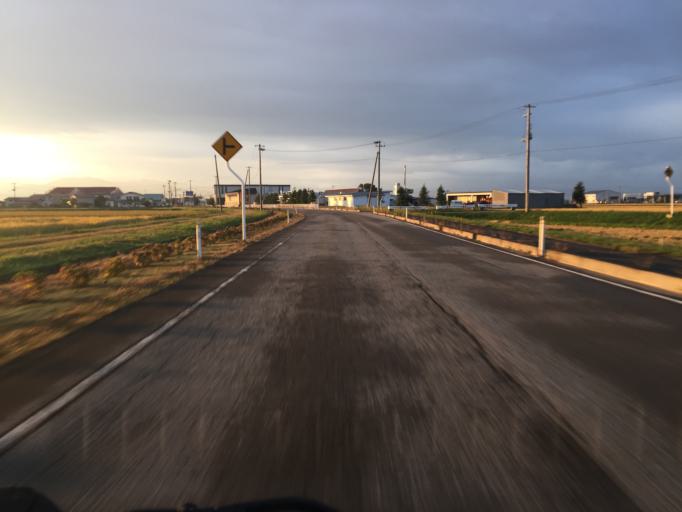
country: JP
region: Fukushima
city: Kitakata
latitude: 37.5573
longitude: 139.8908
